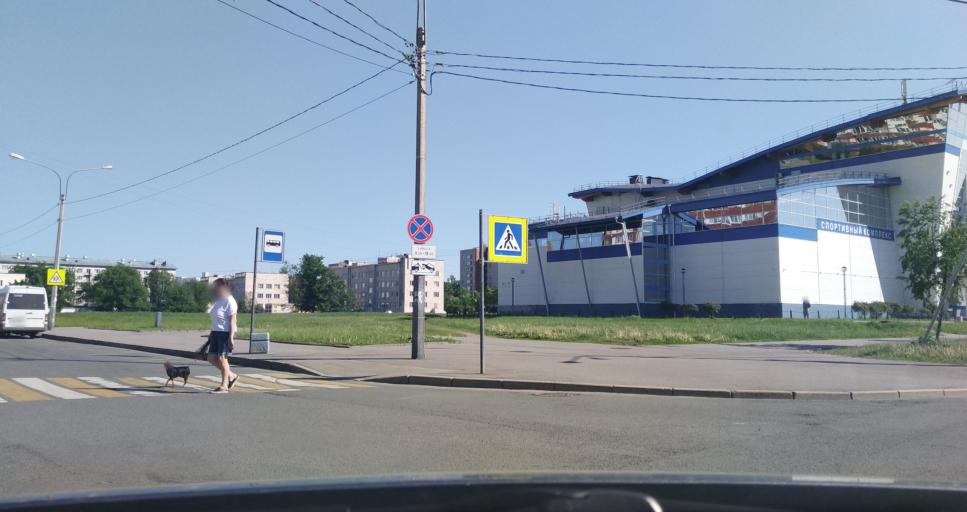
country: RU
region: St.-Petersburg
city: Krasnoye Selo
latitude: 59.7436
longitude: 30.0860
